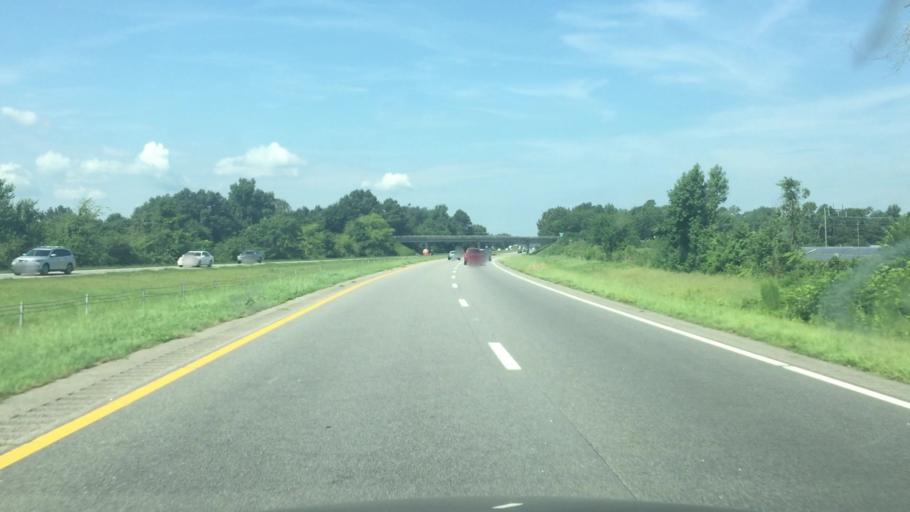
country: US
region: North Carolina
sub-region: Scotland County
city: Laurinburg
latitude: 34.7554
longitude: -79.4422
